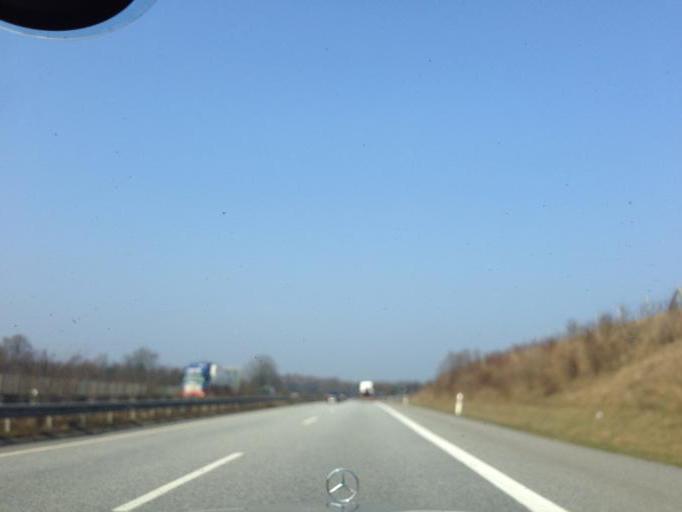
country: DE
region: Schleswig-Holstein
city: Daldorf
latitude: 54.0217
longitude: 10.2440
